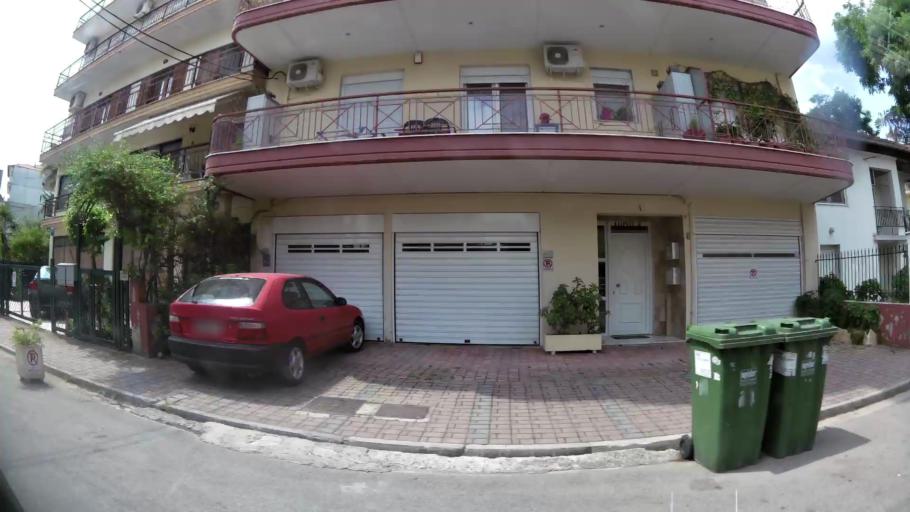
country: GR
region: Central Macedonia
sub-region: Nomos Pierias
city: Katerini
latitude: 40.2760
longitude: 22.5078
